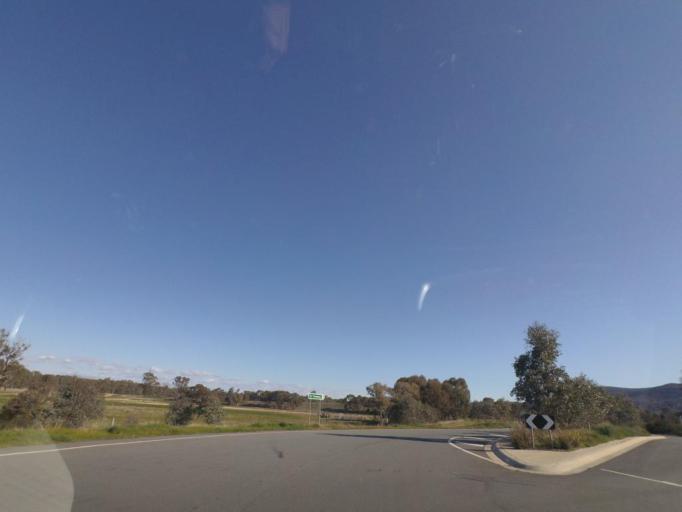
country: AU
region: Victoria
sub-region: Wangaratta
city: Wangaratta
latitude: -36.4246
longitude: 146.2629
